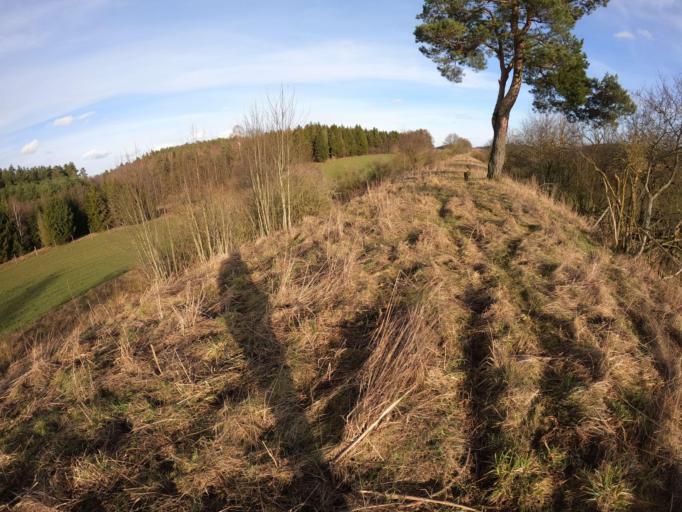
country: PL
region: West Pomeranian Voivodeship
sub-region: Powiat koszalinski
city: Polanow
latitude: 54.2158
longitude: 16.7403
